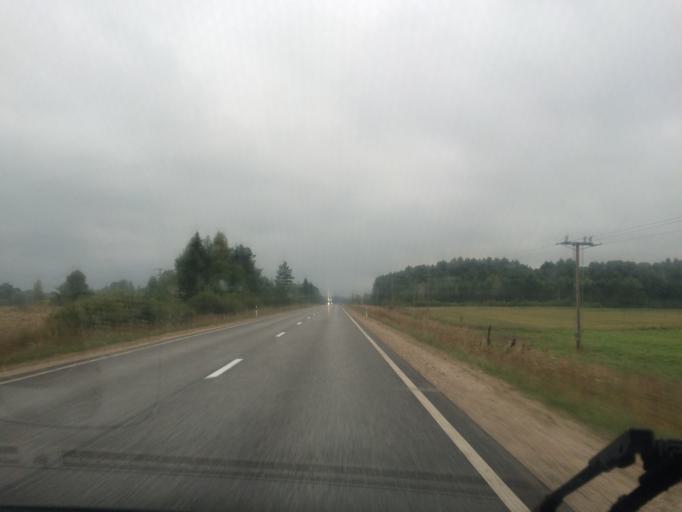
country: LV
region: Livani
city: Livani
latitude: 56.5223
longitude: 26.4396
